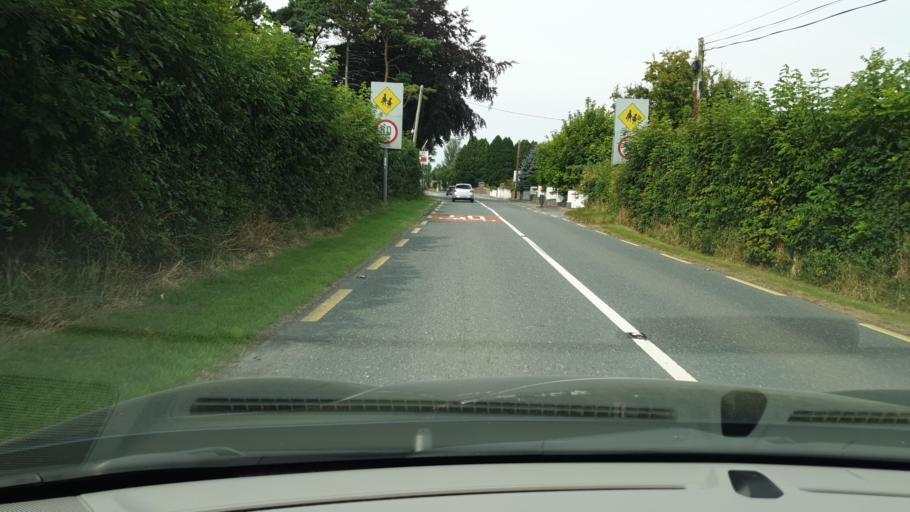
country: IE
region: Leinster
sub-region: An Mhi
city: Athboy
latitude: 53.6462
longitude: -6.8602
